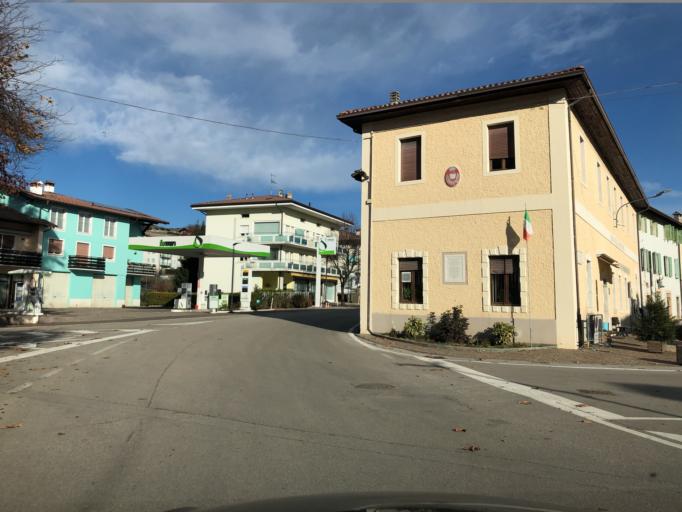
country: IT
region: Trentino-Alto Adige
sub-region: Provincia di Trento
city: Brentonico
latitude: 45.8183
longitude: 10.9570
